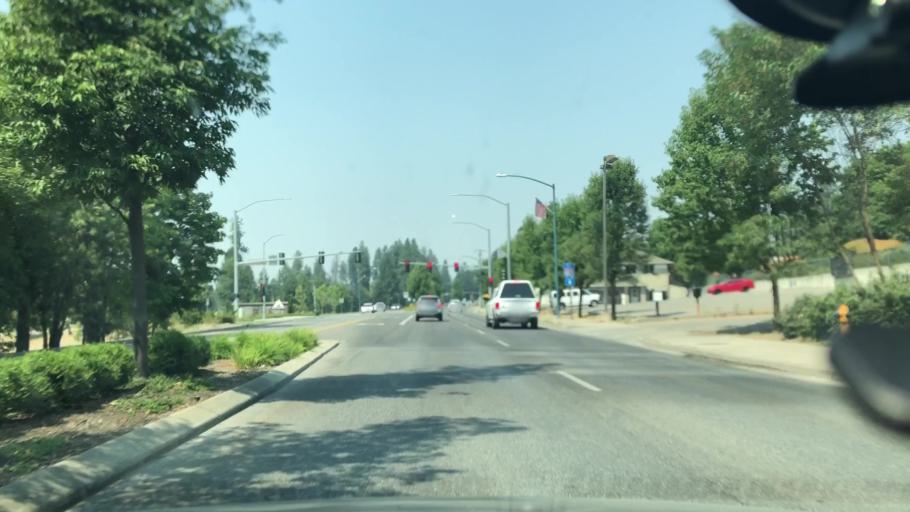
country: US
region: Idaho
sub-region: Kootenai County
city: Coeur d'Alene
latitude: 47.6792
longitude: -116.7907
